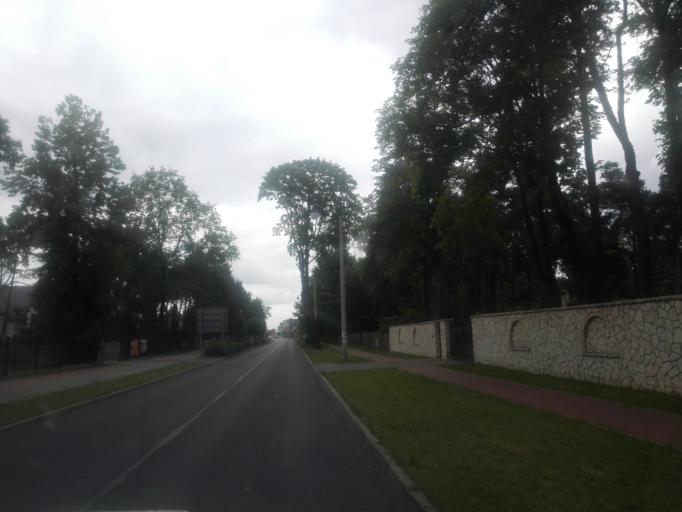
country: PL
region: Silesian Voivodeship
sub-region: Powiat czestochowski
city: Olsztyn
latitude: 50.7457
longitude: 19.2674
